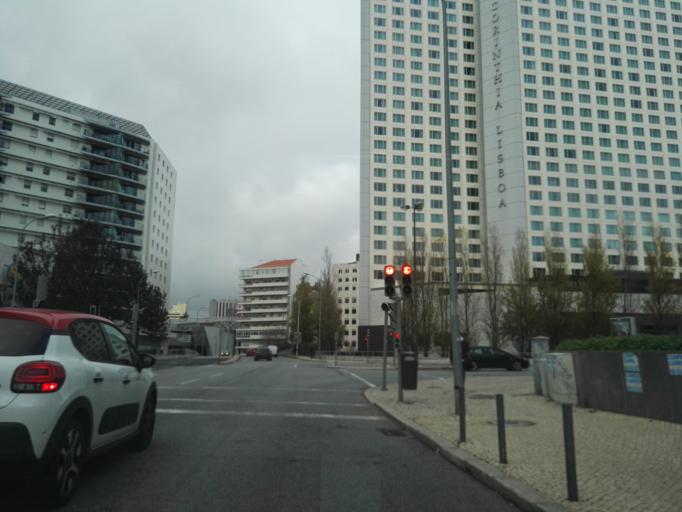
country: PT
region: Lisbon
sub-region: Lisbon
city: Lisbon
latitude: 38.7380
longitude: -9.1675
